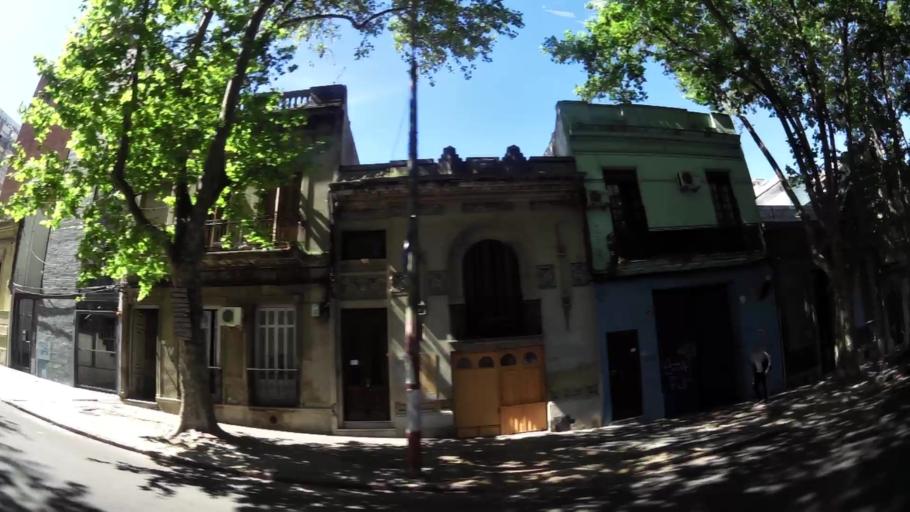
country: UY
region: Montevideo
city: Montevideo
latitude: -34.9121
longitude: -56.1754
